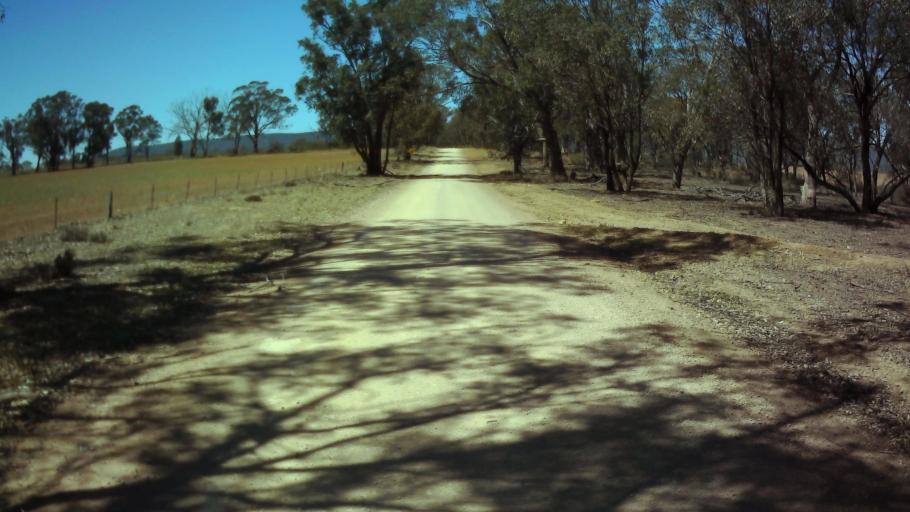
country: AU
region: New South Wales
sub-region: Weddin
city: Grenfell
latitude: -33.9298
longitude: 148.0778
